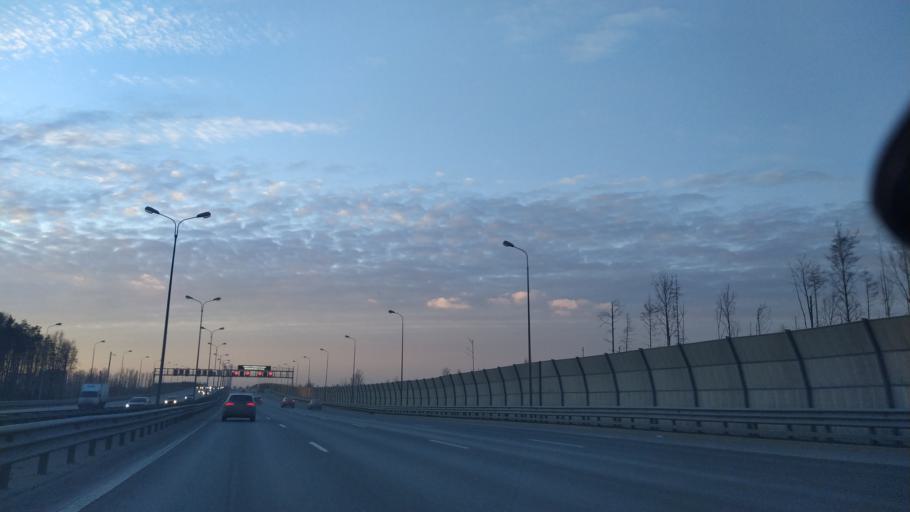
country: RU
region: St.-Petersburg
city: Krasnogvargeisky
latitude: 59.9743
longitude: 30.5416
